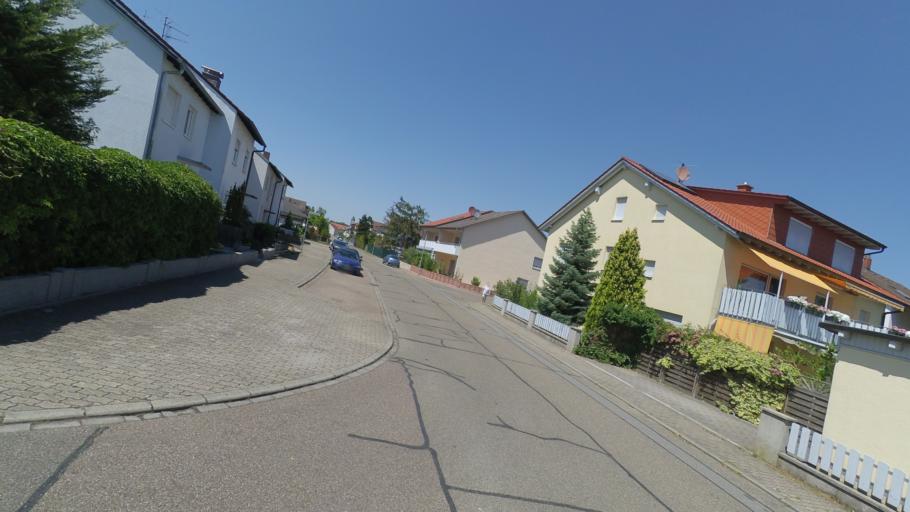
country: DE
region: Baden-Wuerttemberg
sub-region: Karlsruhe Region
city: Ketsch
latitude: 49.3608
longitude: 8.5302
